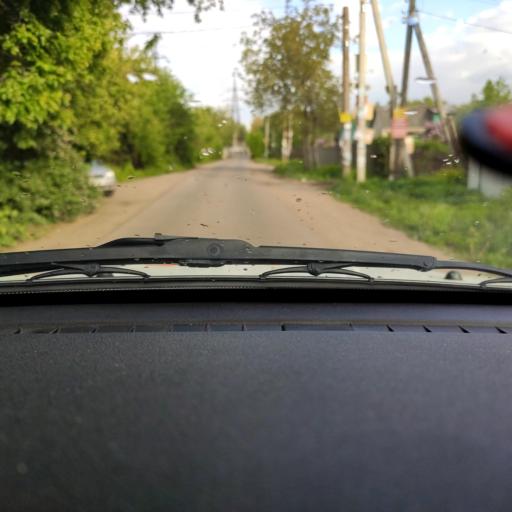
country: RU
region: Voronezj
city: Maslovka
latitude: 51.5840
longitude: 39.1613
